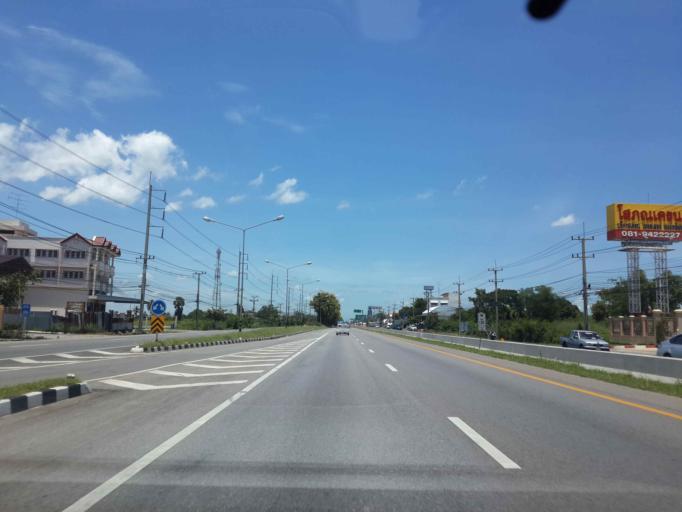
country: TH
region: Phetchaburi
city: Khao Yoi
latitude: 13.2975
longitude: 99.8234
